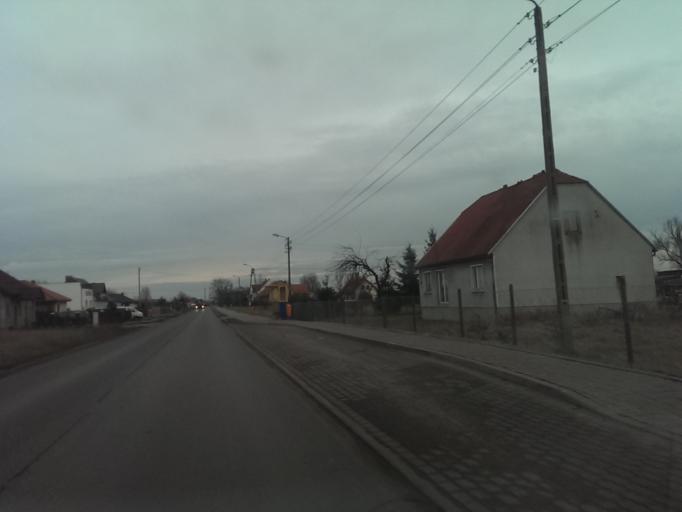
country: PL
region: Kujawsko-Pomorskie
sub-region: Powiat nakielski
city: Szubin
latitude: 53.0724
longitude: 17.8137
